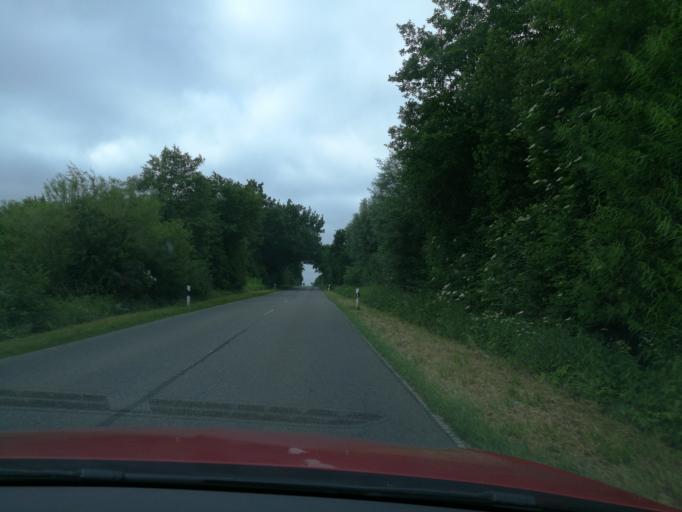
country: DE
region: Schleswig-Holstein
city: Politz
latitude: 53.7906
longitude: 10.3815
